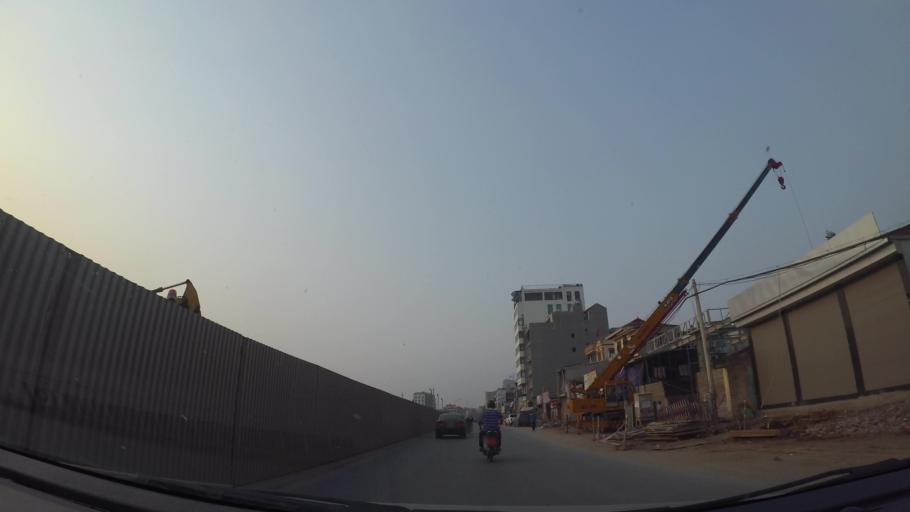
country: VN
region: Ha Noi
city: Tay Ho
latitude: 21.0718
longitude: 105.7857
